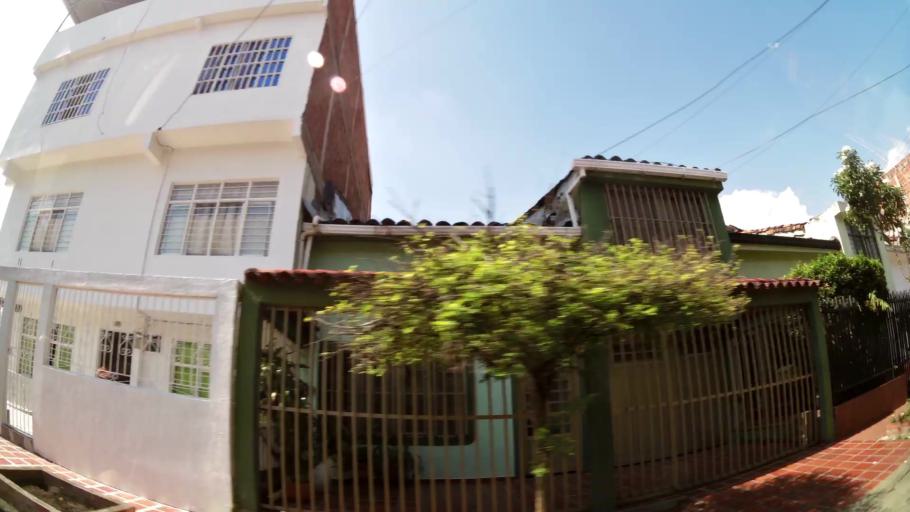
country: CO
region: Valle del Cauca
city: Cali
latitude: 3.4230
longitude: -76.5308
